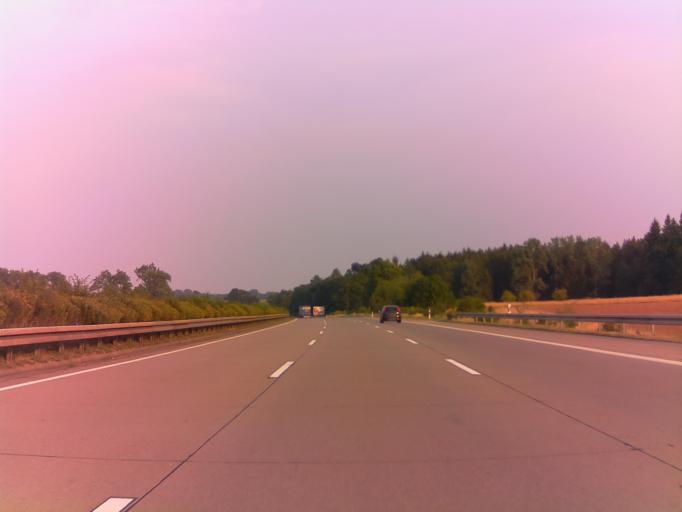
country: DE
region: Thuringia
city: Mechterstadt
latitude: 50.9265
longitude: 10.5130
